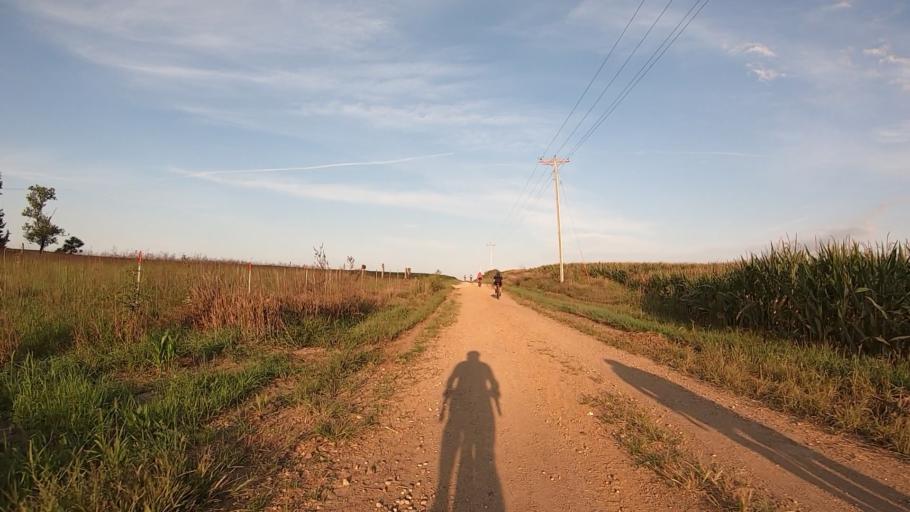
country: US
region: Kansas
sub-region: Marshall County
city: Marysville
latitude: 39.7694
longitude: -96.7190
